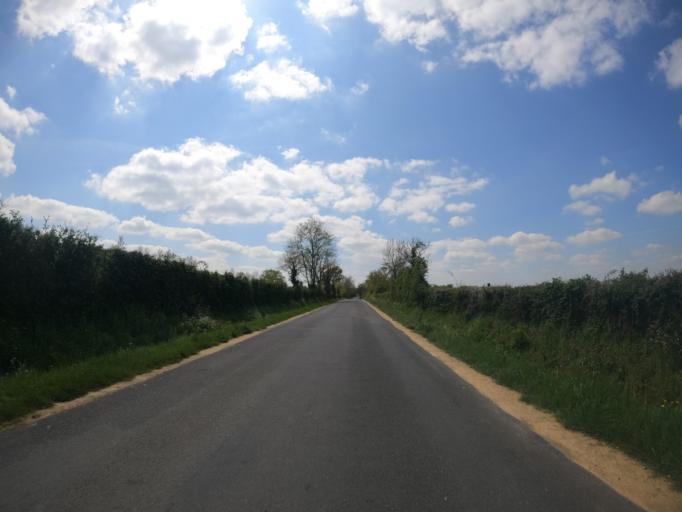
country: FR
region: Poitou-Charentes
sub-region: Departement des Deux-Sevres
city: Saint-Varent
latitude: 46.8314
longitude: -0.2631
